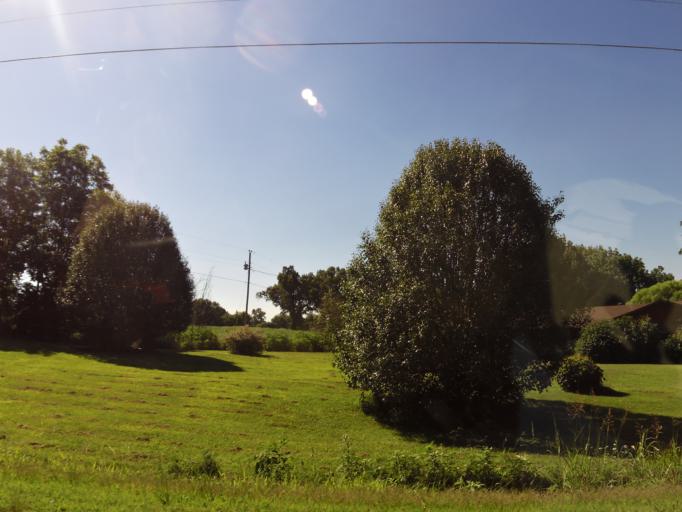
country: US
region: Arkansas
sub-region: Clay County
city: Piggott
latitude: 36.4321
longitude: -90.2652
